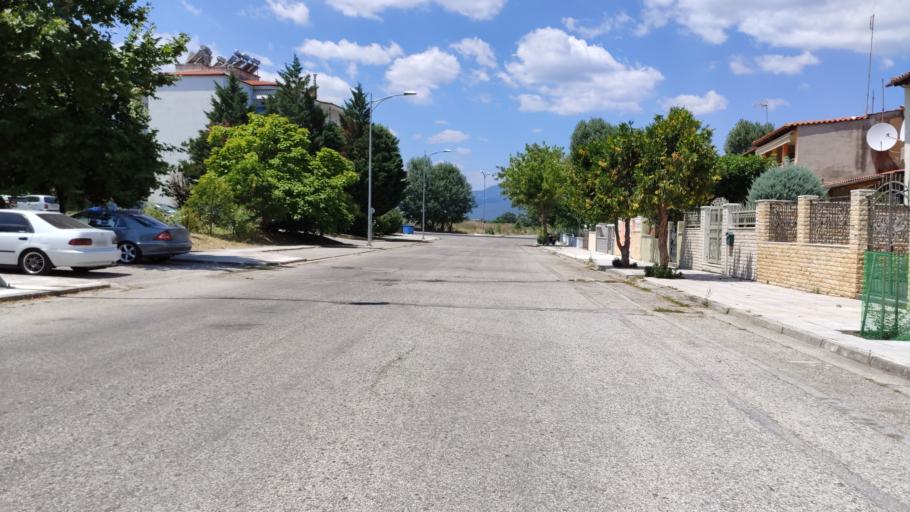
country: GR
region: East Macedonia and Thrace
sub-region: Nomos Rodopis
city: Komotini
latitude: 41.1267
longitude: 25.3954
